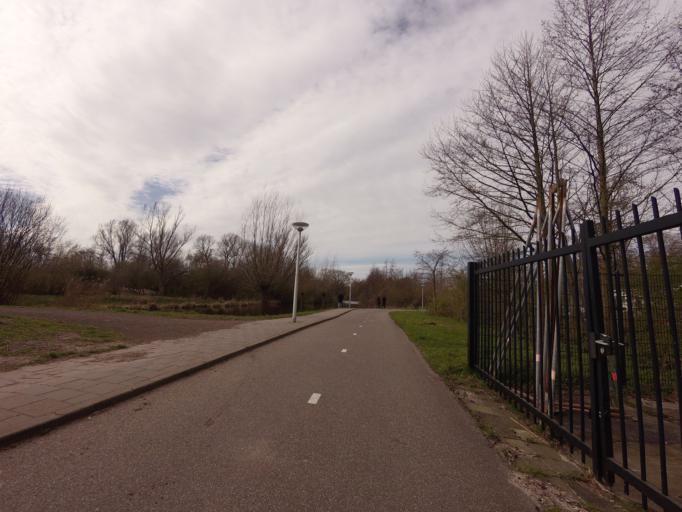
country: NL
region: North Holland
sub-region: Gemeente Amstelveen
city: Amstelveen
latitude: 52.3033
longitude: 4.8419
